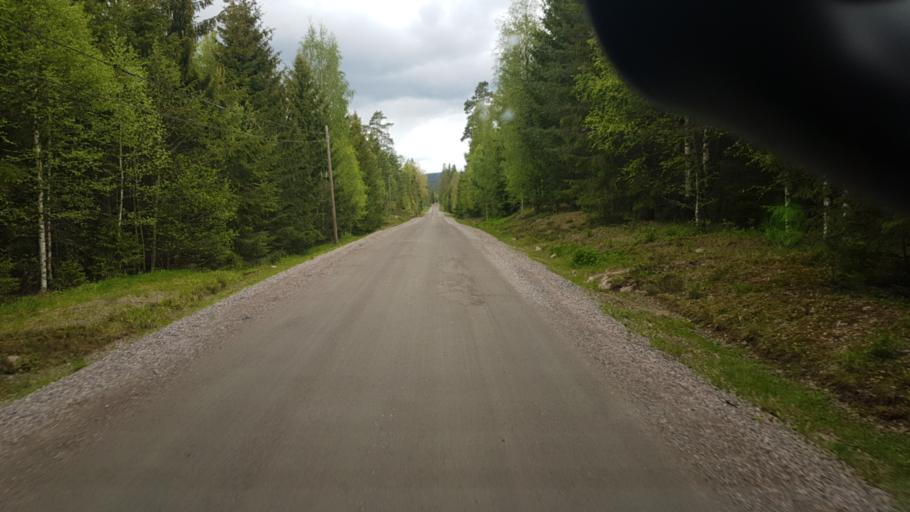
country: SE
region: Vaermland
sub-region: Eda Kommun
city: Charlottenberg
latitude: 59.9598
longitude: 12.5099
